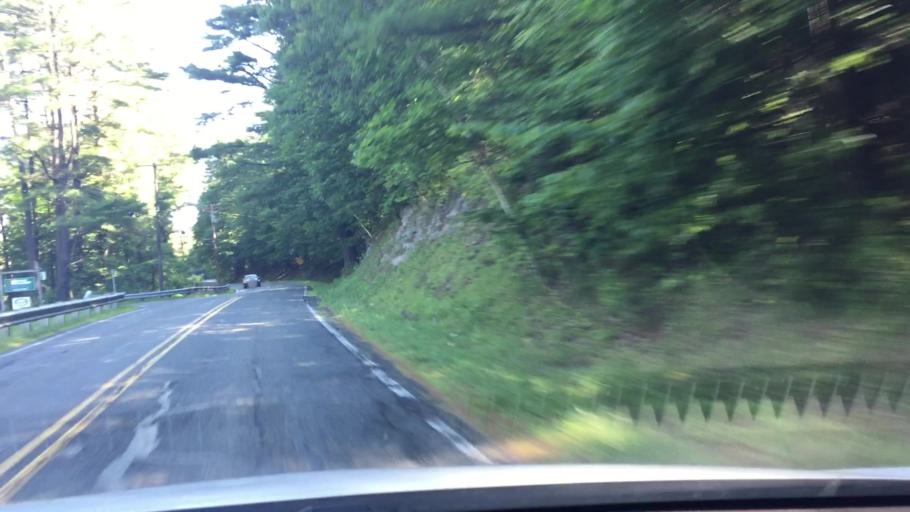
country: US
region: Massachusetts
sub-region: Berkshire County
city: West Stockbridge
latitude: 42.3171
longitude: -73.3693
